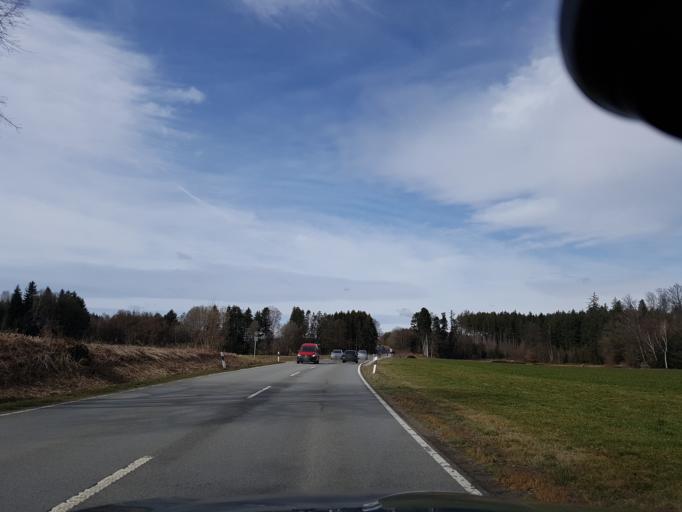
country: DE
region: Bavaria
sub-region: Upper Bavaria
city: Bruckmuhl
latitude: 47.8929
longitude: 11.9010
